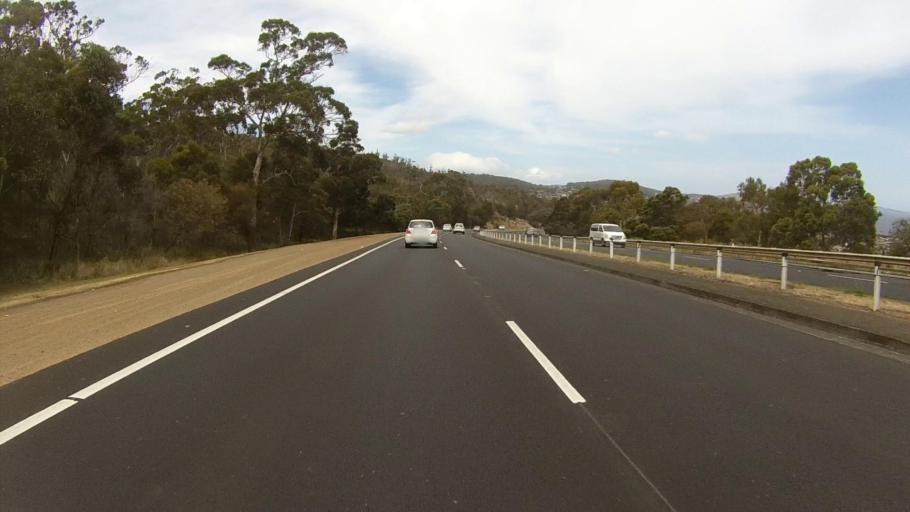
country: AU
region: Tasmania
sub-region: Clarence
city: Warrane
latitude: -42.8670
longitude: 147.3956
